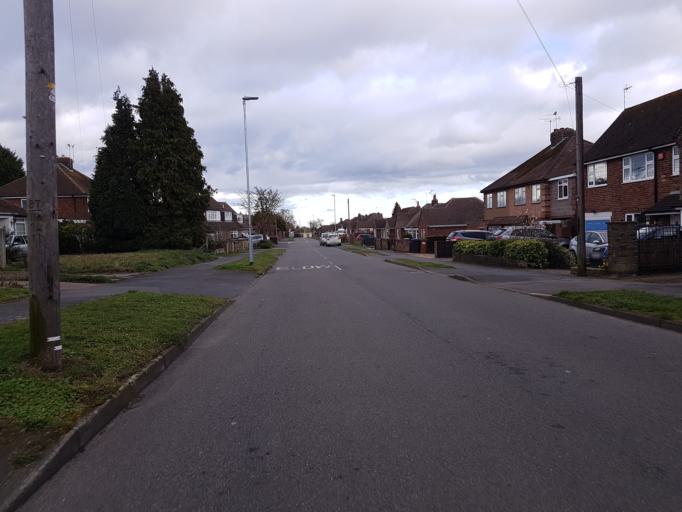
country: GB
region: England
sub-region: Leicestershire
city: Earl Shilton
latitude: 52.5715
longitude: -1.3250
